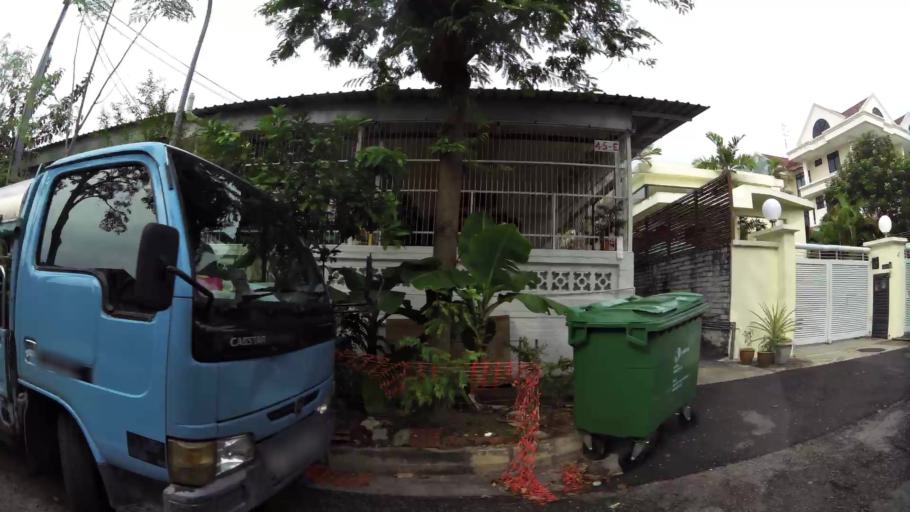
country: SG
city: Singapore
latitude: 1.3496
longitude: 103.8829
